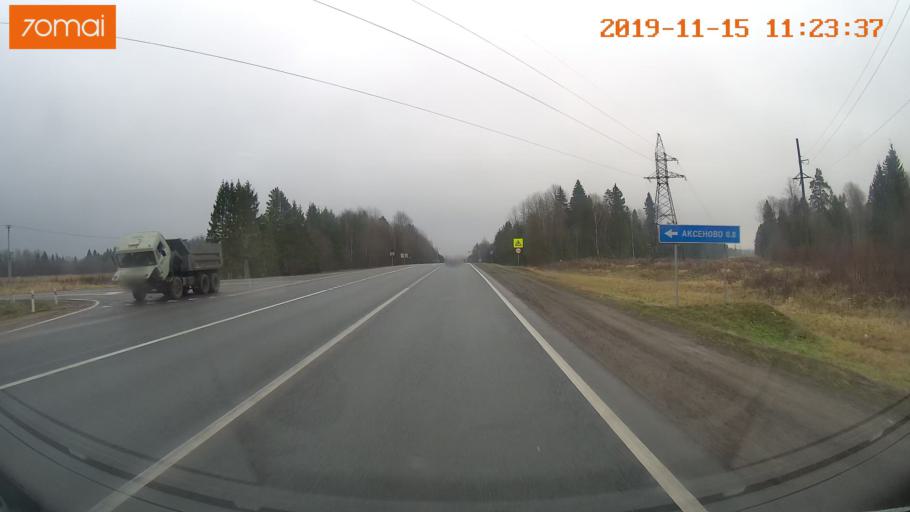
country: RU
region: Vologda
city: Molochnoye
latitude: 59.1526
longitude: 39.3864
